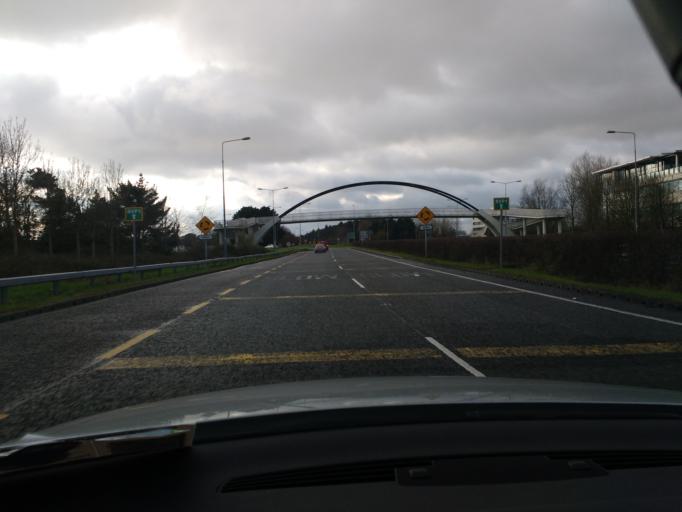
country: IE
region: Munster
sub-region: An Clar
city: Shannon
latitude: 52.7042
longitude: -8.8921
